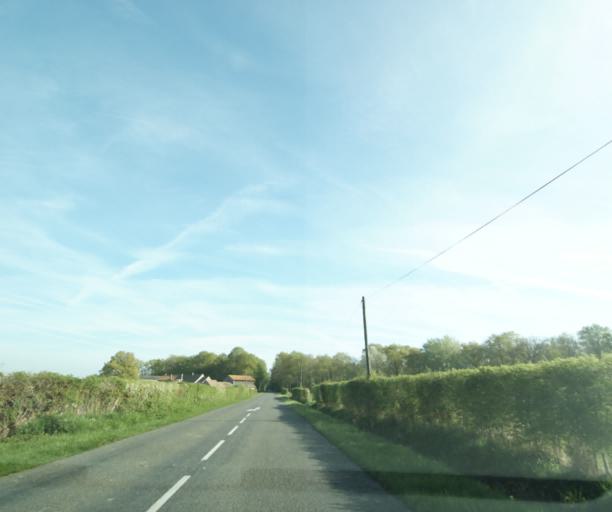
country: FR
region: Ile-de-France
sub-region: Departement de Seine-et-Marne
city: Vernou-la-Celle-sur-Seine
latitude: 48.4416
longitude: 2.8567
